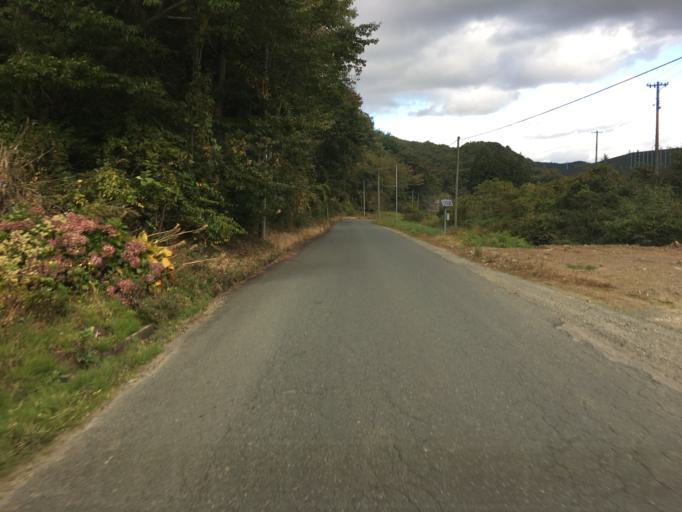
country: JP
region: Fukushima
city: Yanagawamachi-saiwaicho
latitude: 37.7763
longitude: 140.7130
